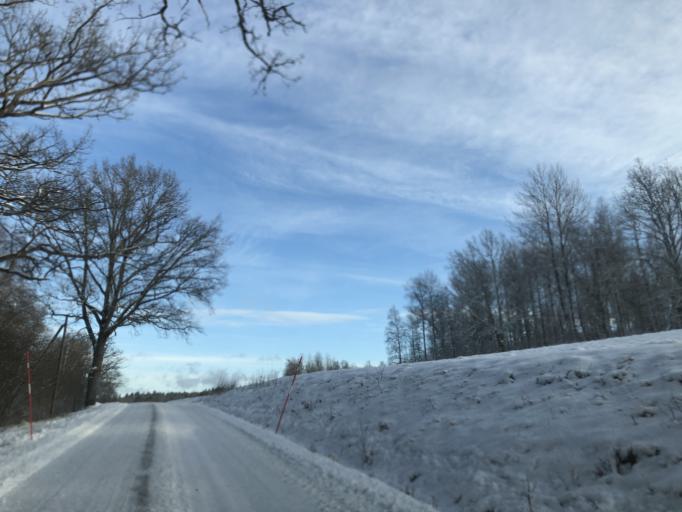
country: SE
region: Vaestra Goetaland
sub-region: Ulricehamns Kommun
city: Ulricehamn
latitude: 57.7269
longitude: 13.4623
